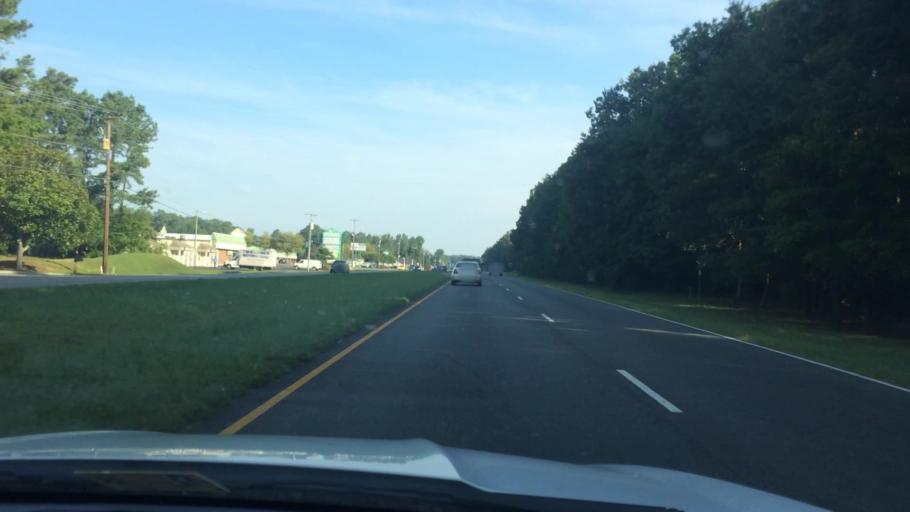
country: US
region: Virginia
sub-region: Gloucester County
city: Gloucester Courthouse
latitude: 37.3374
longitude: -76.5170
